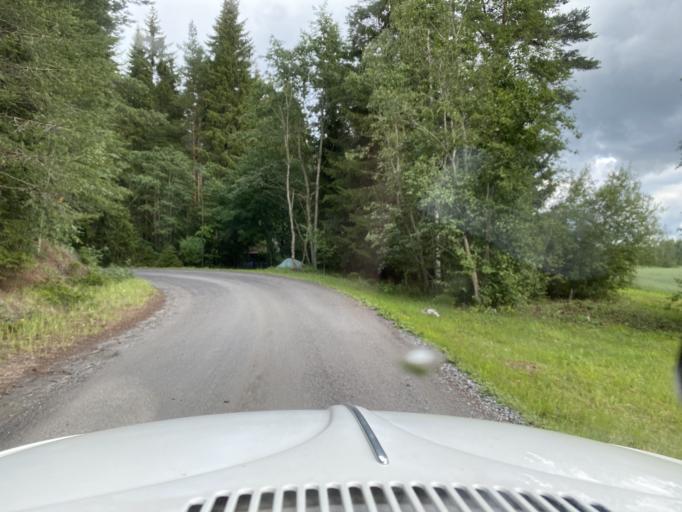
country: FI
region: Pirkanmaa
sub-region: Lounais-Pirkanmaa
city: Punkalaidun
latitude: 61.1297
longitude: 23.0657
